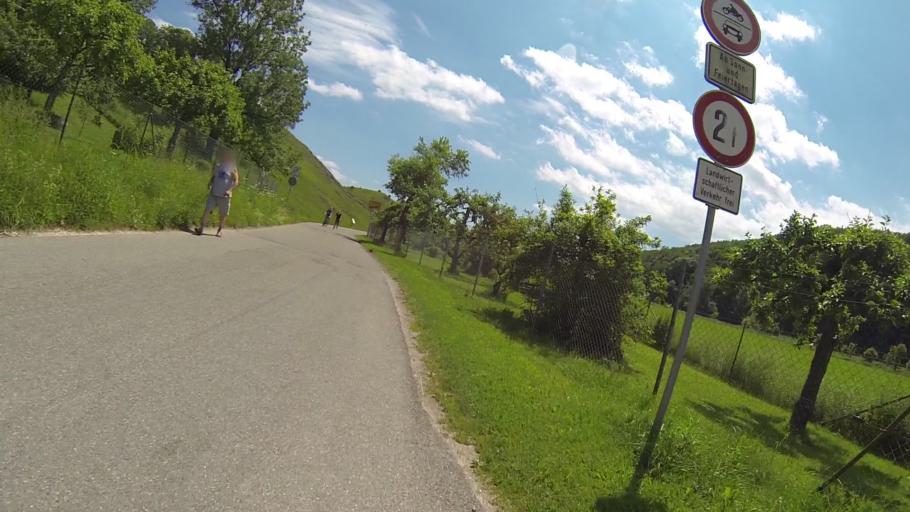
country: DE
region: Baden-Wuerttemberg
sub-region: Regierungsbezirk Stuttgart
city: Herbrechtingen
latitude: 48.6154
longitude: 10.1765
